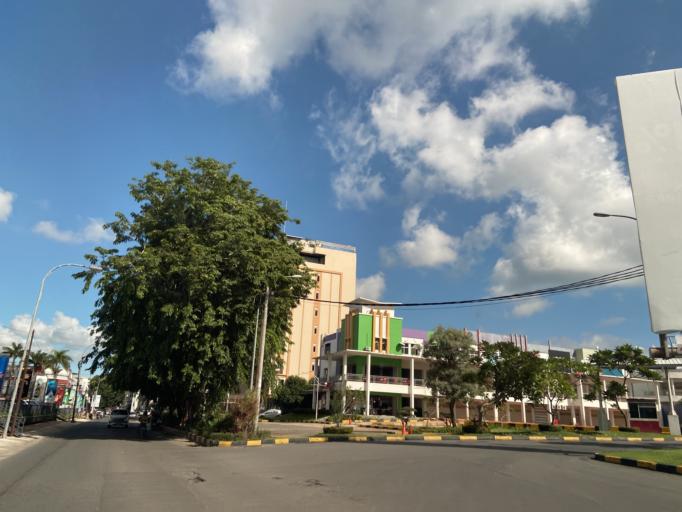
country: SG
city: Singapore
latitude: 1.1421
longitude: 104.0075
